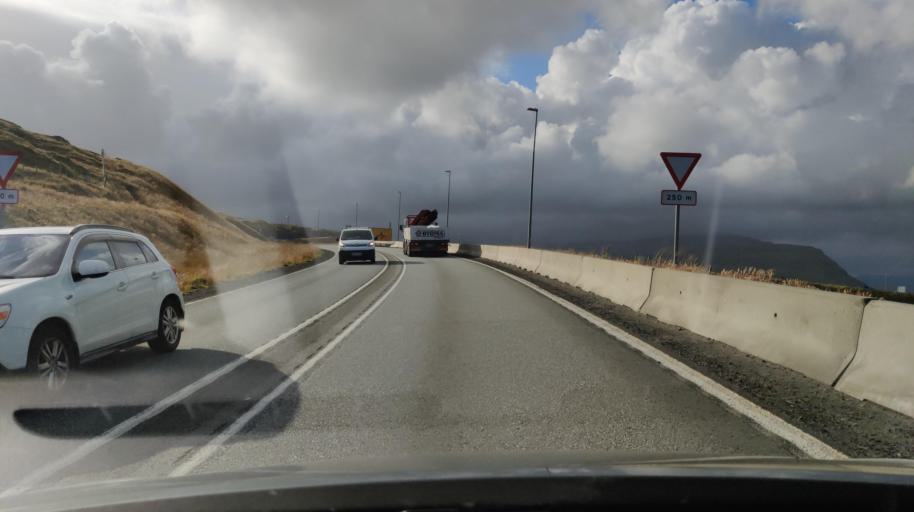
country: FO
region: Streymoy
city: Hoyvik
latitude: 62.0433
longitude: -6.7744
